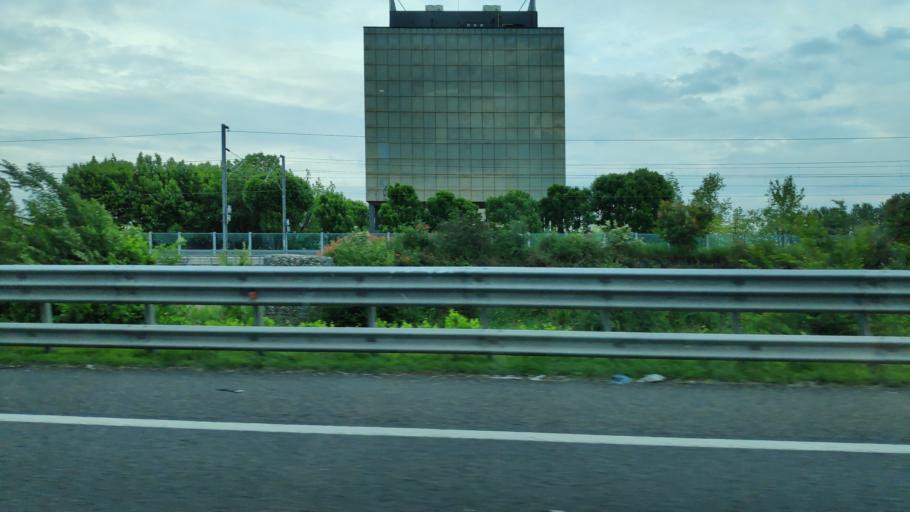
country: IT
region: Emilia-Romagna
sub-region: Provincia di Reggio Emilia
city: Reggio nell'Emilia
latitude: 44.7309
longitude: 10.6218
